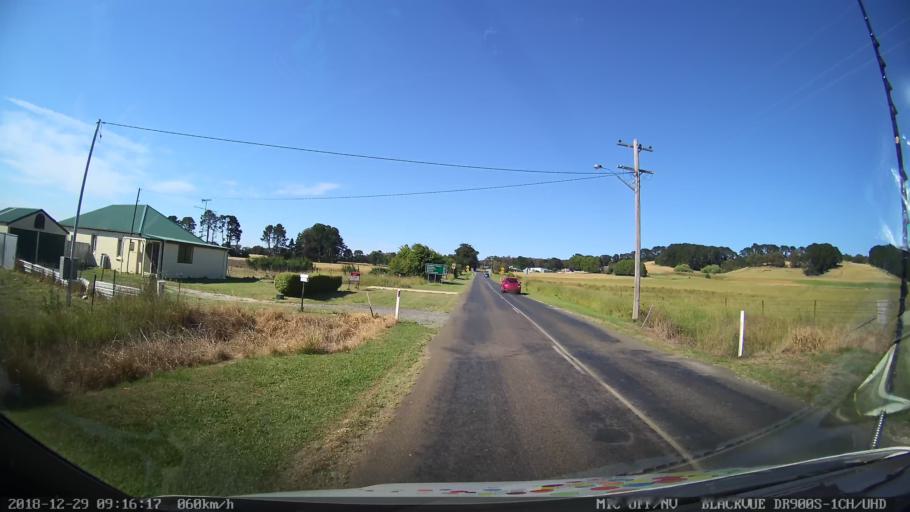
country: AU
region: New South Wales
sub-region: Upper Lachlan Shire
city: Crookwell
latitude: -34.4575
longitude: 149.4527
